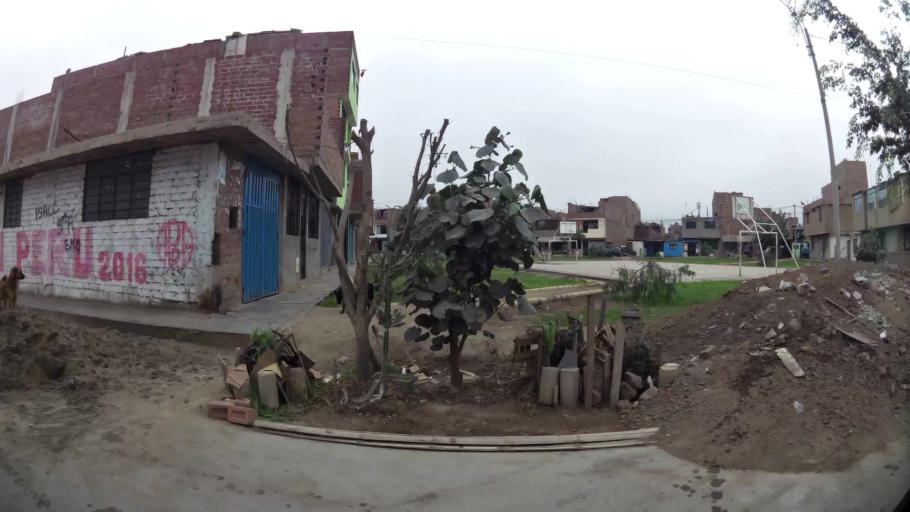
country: PE
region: Lima
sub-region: Lima
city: Independencia
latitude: -11.9543
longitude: -77.0808
